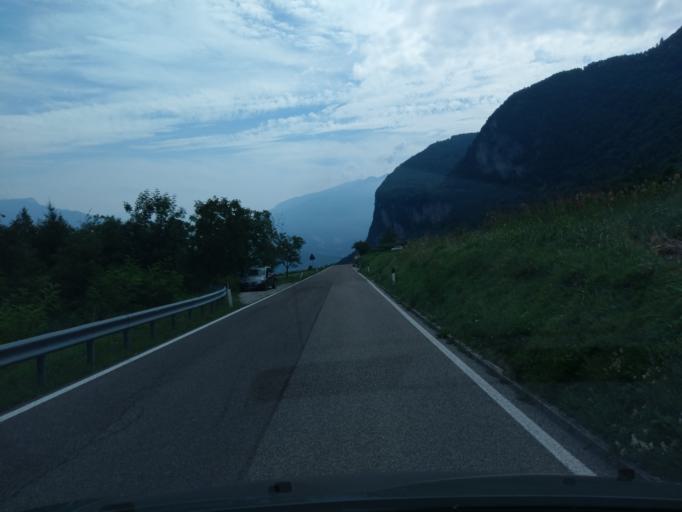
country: IT
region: Trentino-Alto Adige
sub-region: Provincia di Trento
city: Tenno
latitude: 45.9273
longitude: 10.8163
